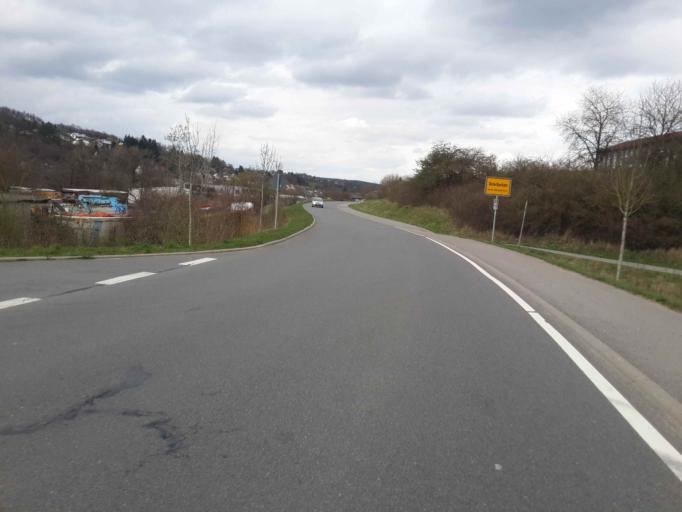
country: DE
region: Baden-Wuerttemberg
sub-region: Karlsruhe Region
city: Osterburken
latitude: 49.4195
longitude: 9.4135
